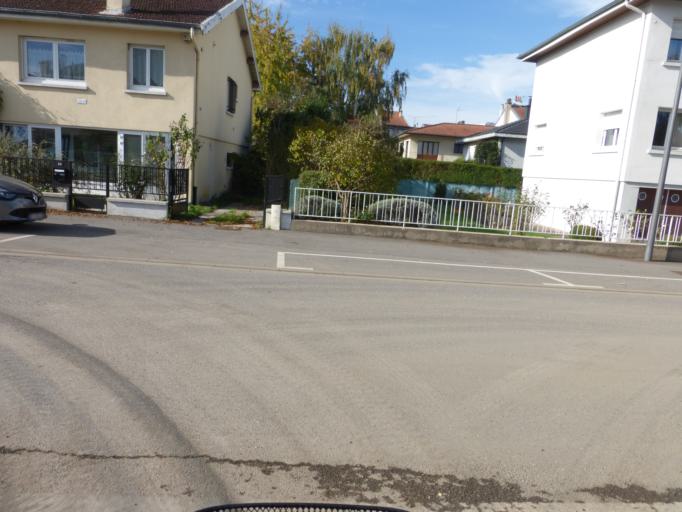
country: FR
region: Lorraine
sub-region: Departement de Meurthe-et-Moselle
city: Villers-les-Nancy
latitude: 48.6753
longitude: 6.1555
